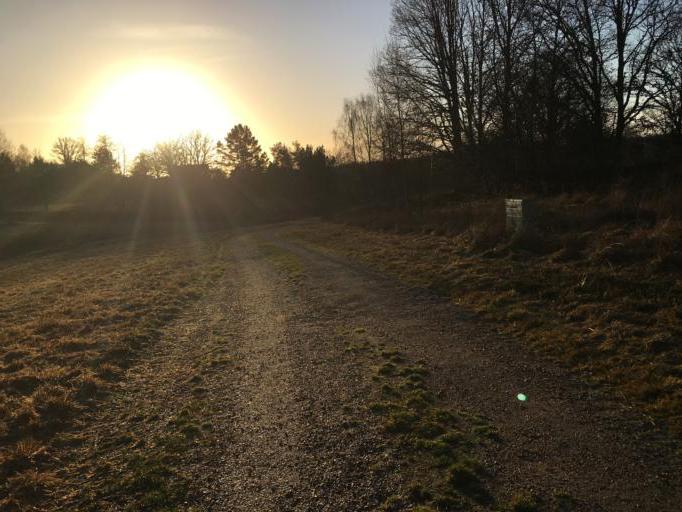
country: SE
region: Kalmar
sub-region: Vasterviks Kommun
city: Vaestervik
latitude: 57.6278
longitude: 16.5289
